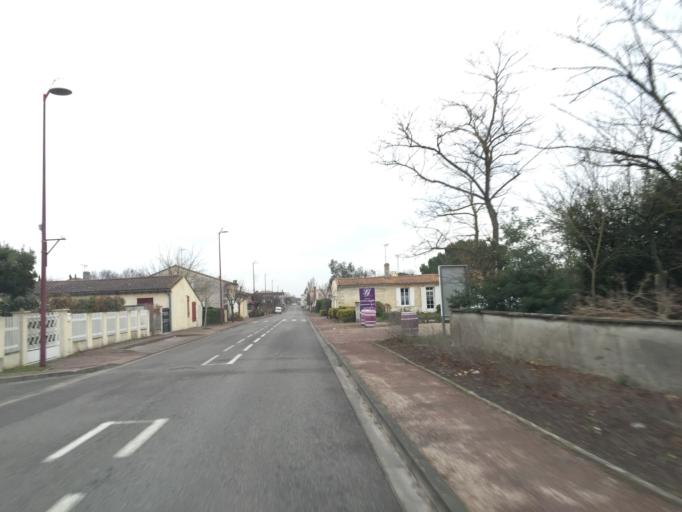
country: FR
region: Aquitaine
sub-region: Departement de la Gironde
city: Cussac-Fort-Medoc
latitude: 45.1169
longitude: -0.7313
